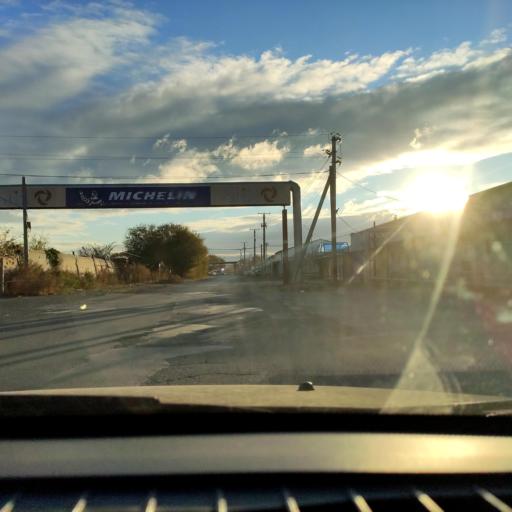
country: RU
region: Samara
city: Tol'yatti
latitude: 53.5758
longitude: 49.2789
